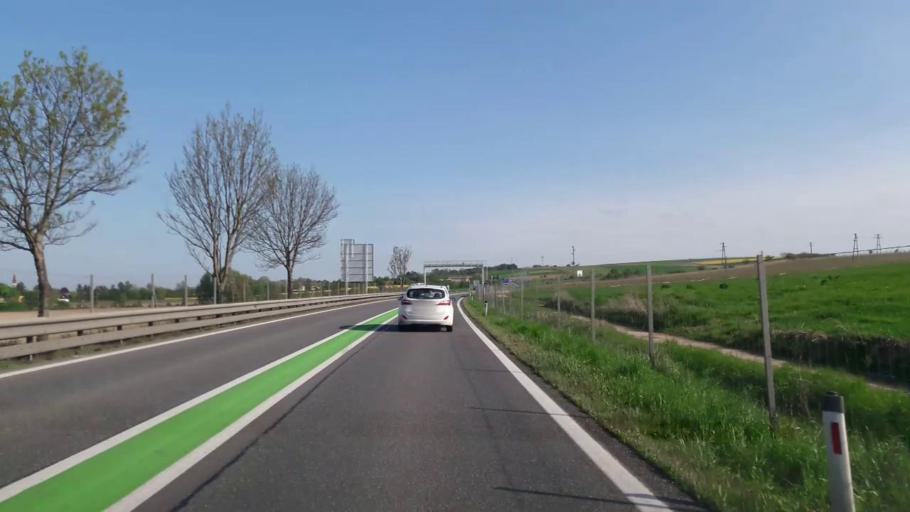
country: AT
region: Lower Austria
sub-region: Politischer Bezirk Hollabrunn
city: Gollersdorf
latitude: 48.4999
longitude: 16.1047
